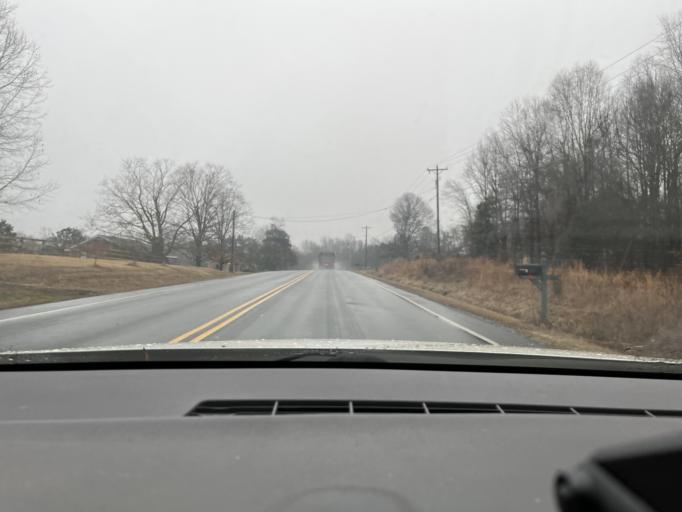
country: US
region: North Carolina
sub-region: Guilford County
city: Pleasant Garden
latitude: 35.9988
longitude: -79.7458
